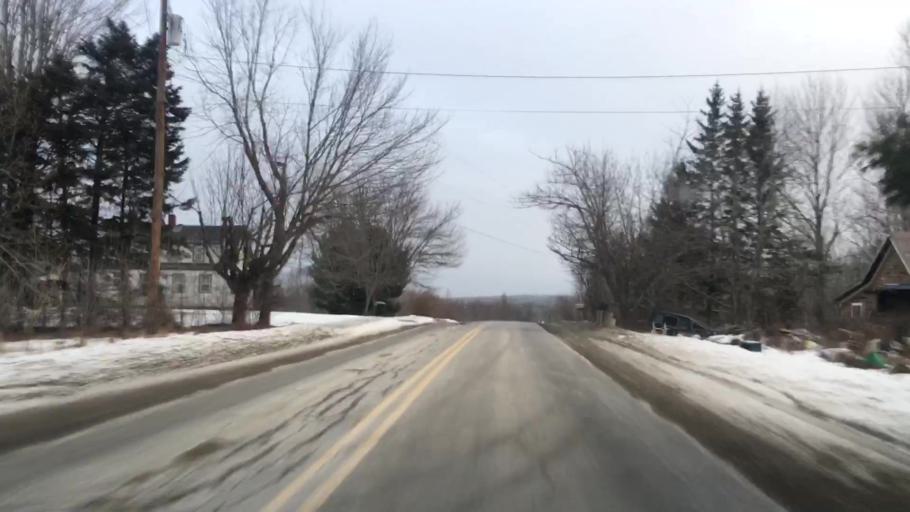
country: US
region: Maine
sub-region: Hancock County
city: Franklin
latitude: 44.6828
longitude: -68.3516
